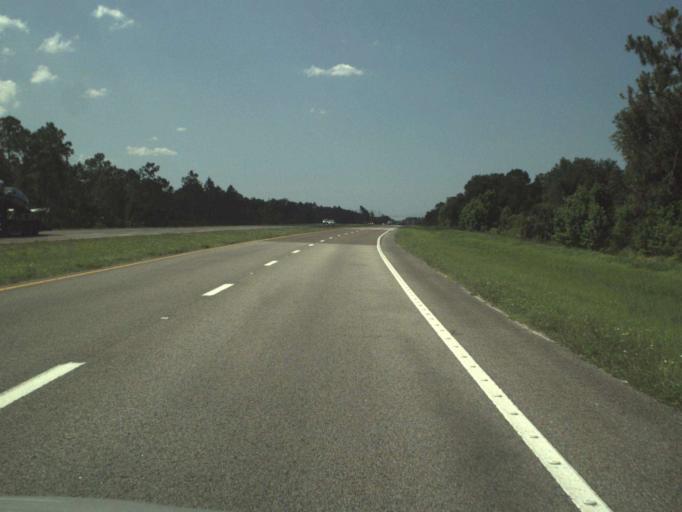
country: US
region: Florida
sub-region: Orange County
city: Christmas
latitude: 28.3966
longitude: -80.9450
